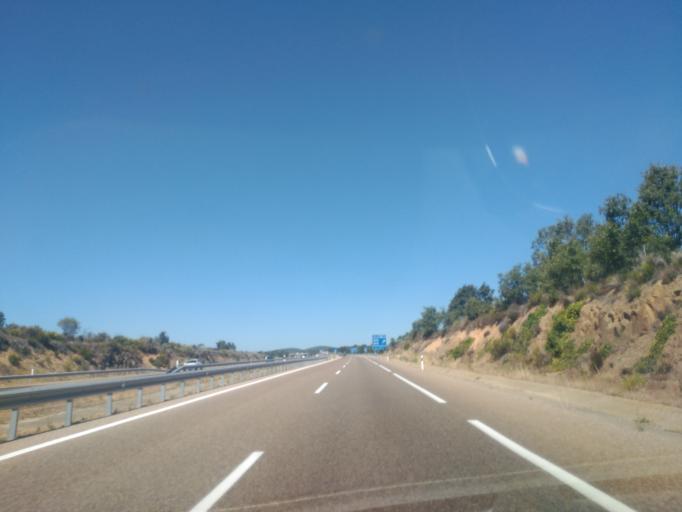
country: ES
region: Castille and Leon
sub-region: Provincia de Zamora
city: Mombuey
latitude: 42.0125
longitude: -6.2948
